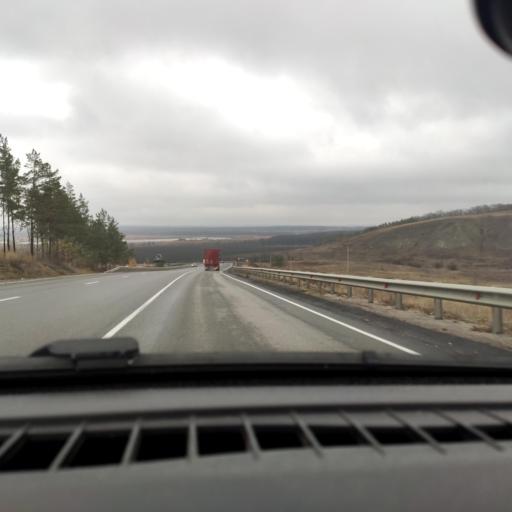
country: RU
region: Voronezj
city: Ostrogozhsk
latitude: 51.0238
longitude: 38.9833
